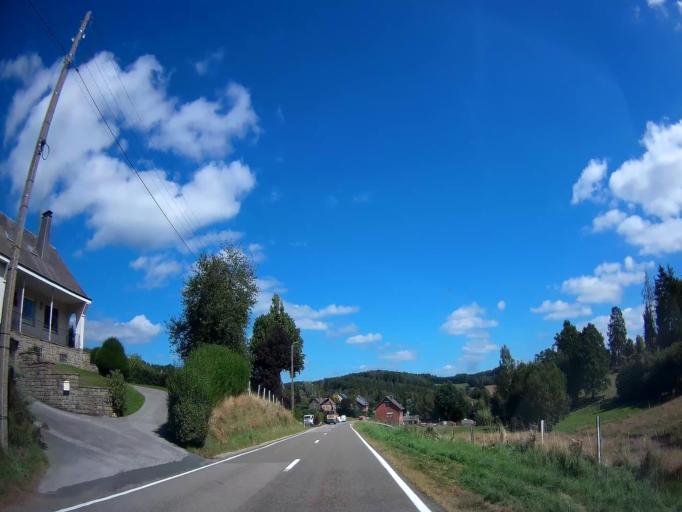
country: BE
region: Wallonia
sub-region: Province du Luxembourg
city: Bertogne
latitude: 50.0888
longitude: 5.6712
